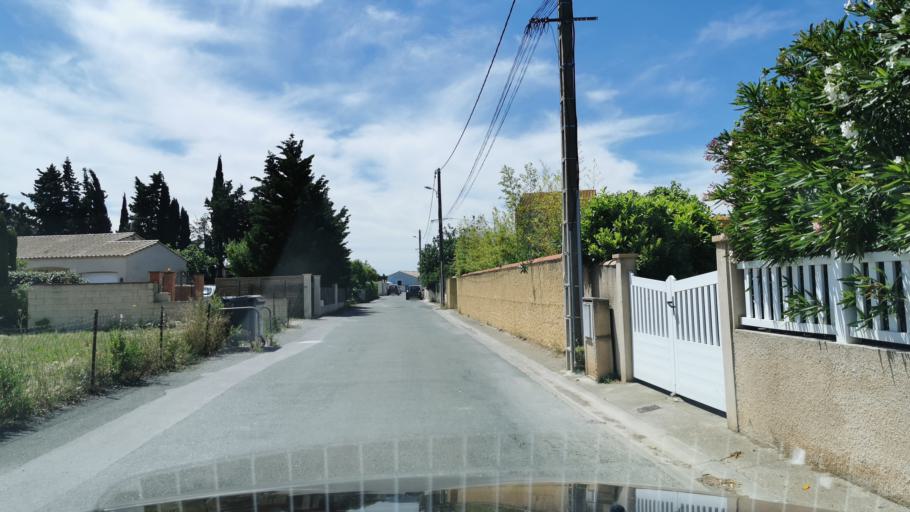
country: FR
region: Languedoc-Roussillon
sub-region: Departement de l'Aude
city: Canet
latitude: 43.2157
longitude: 2.8554
